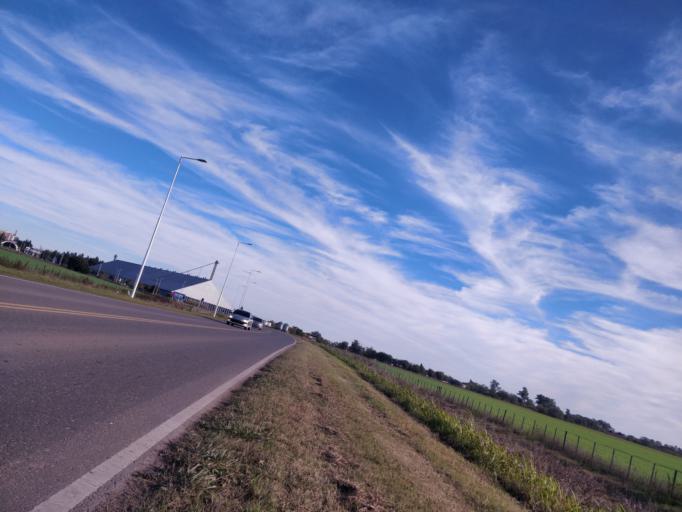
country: AR
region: Cordoba
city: Leones
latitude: -32.6476
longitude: -62.2924
